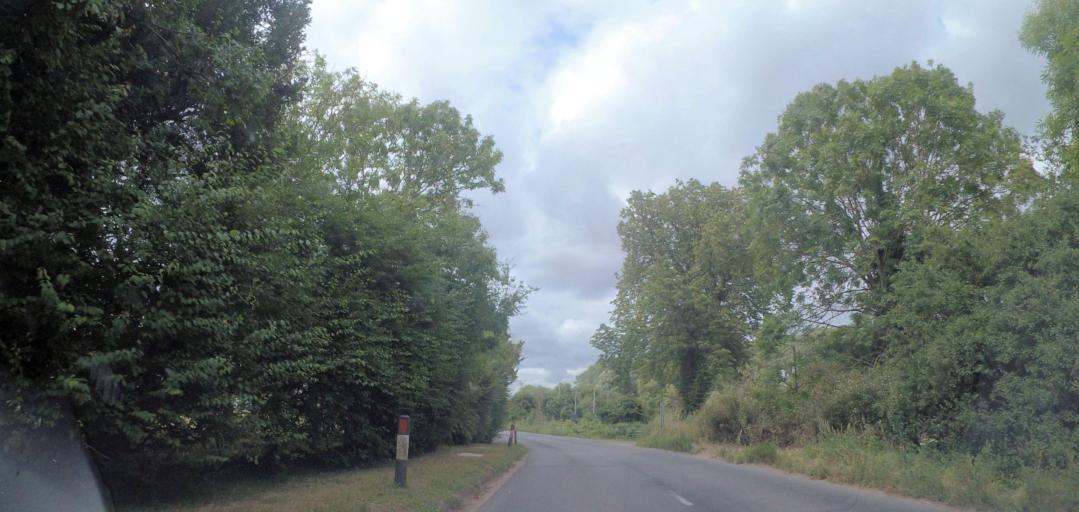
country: GB
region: England
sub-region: Suffolk
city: Lakenheath
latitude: 52.3334
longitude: 0.5343
